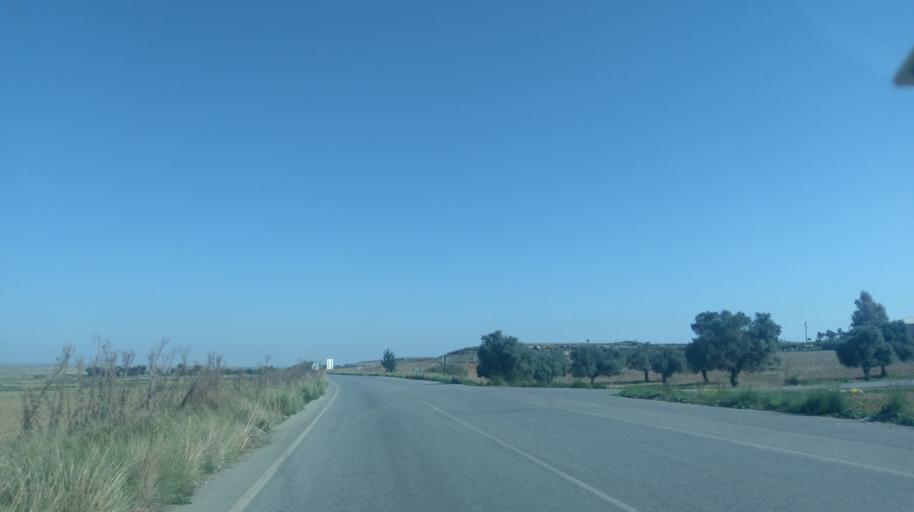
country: CY
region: Ammochostos
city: Lefkonoiko
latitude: 35.2647
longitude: 33.7955
